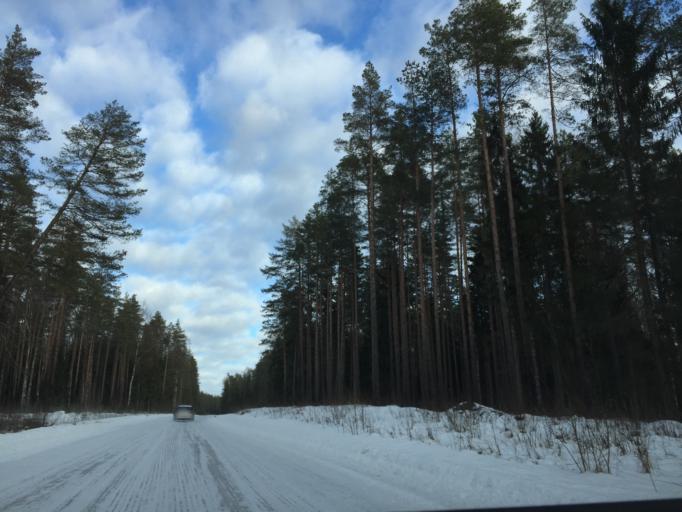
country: LV
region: Ogre
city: Jumprava
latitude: 56.5524
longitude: 24.8975
